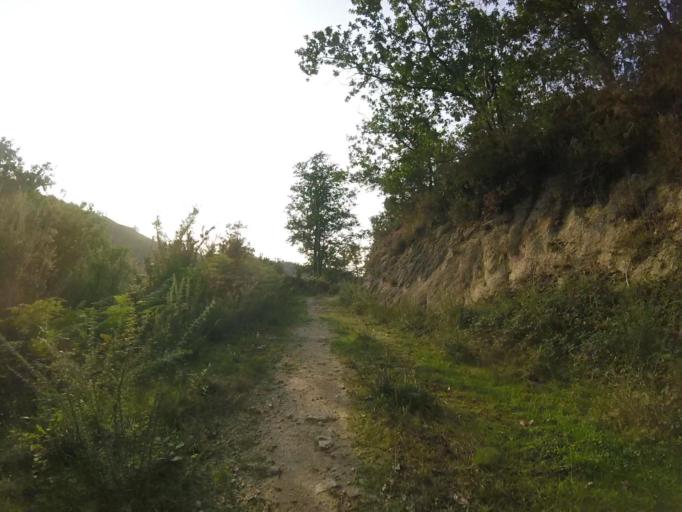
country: ES
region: Navarre
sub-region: Provincia de Navarra
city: Arano
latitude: 43.2539
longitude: -1.8403
